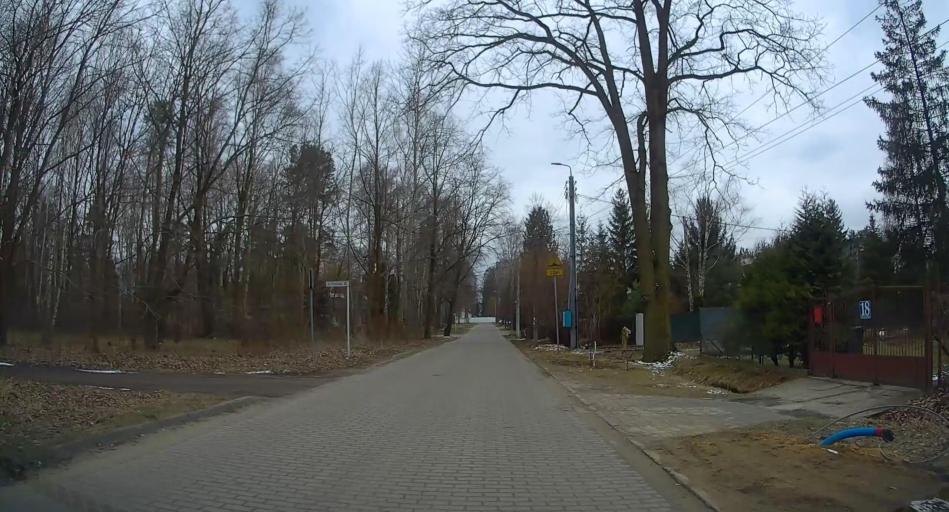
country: PL
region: Masovian Voivodeship
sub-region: Powiat piaseczynski
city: Piaseczno
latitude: 52.0626
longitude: 20.9930
